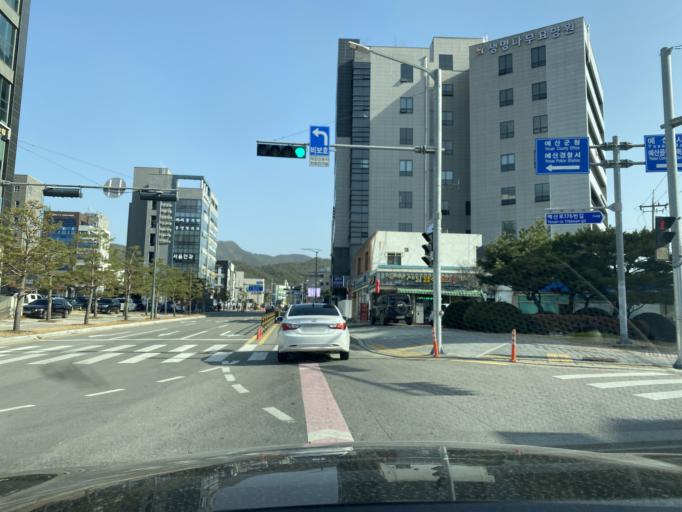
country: KR
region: Chungcheongnam-do
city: Yesan
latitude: 36.6787
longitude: 126.8447
